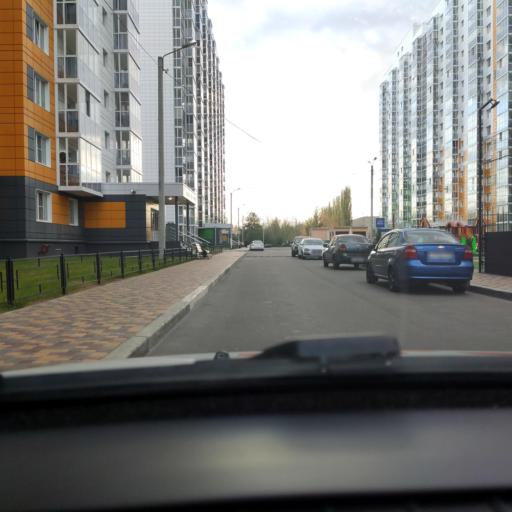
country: RU
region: Voronezj
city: Podgornoye
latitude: 51.7596
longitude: 39.1833
